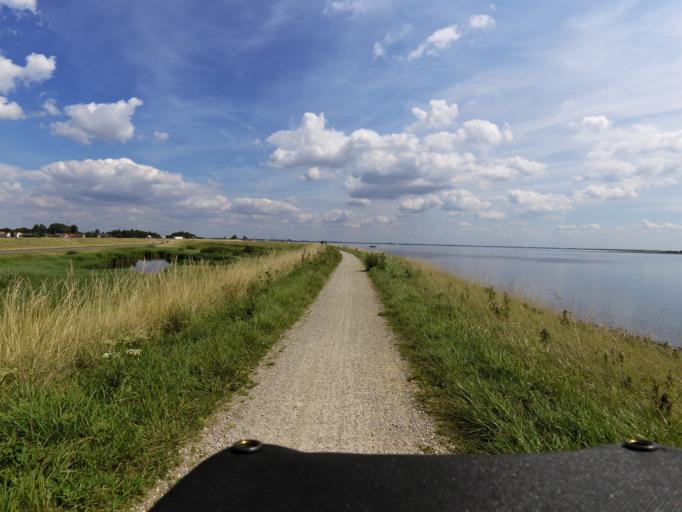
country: NL
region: South Holland
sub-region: Gemeente Goeree-Overflakkee
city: Ouddorp
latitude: 51.7970
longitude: 3.9223
